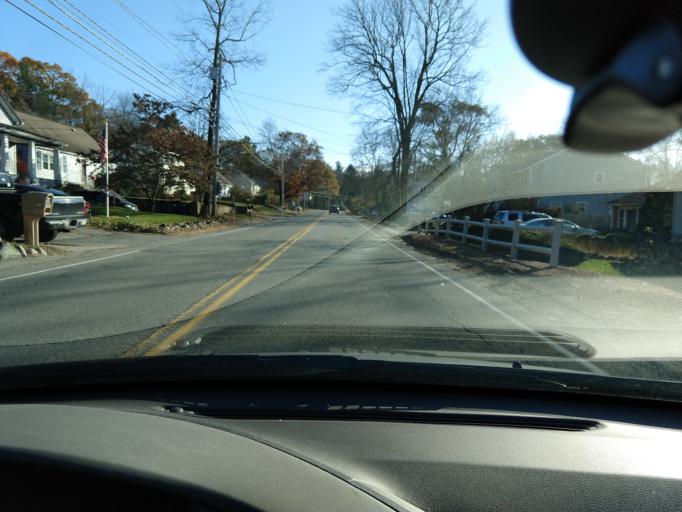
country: US
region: Massachusetts
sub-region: Middlesex County
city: Billerica
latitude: 42.5301
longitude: -71.2842
